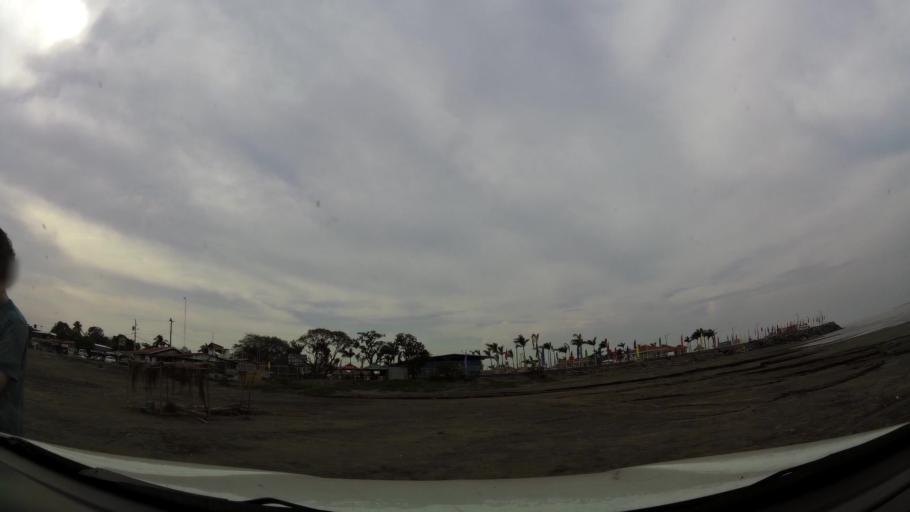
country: NI
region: Rivas
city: San Jorge
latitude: 11.4591
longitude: -85.7902
